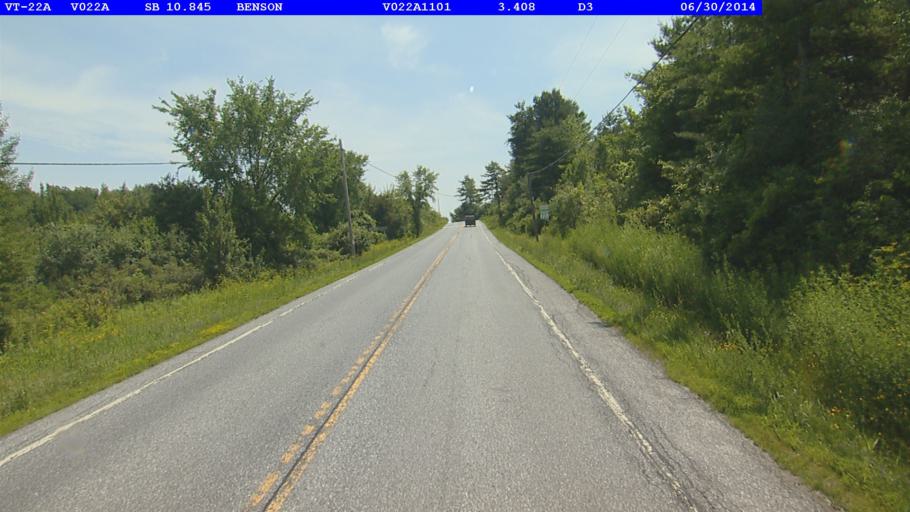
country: US
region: Vermont
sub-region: Rutland County
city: Fair Haven
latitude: 43.7174
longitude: -73.2988
